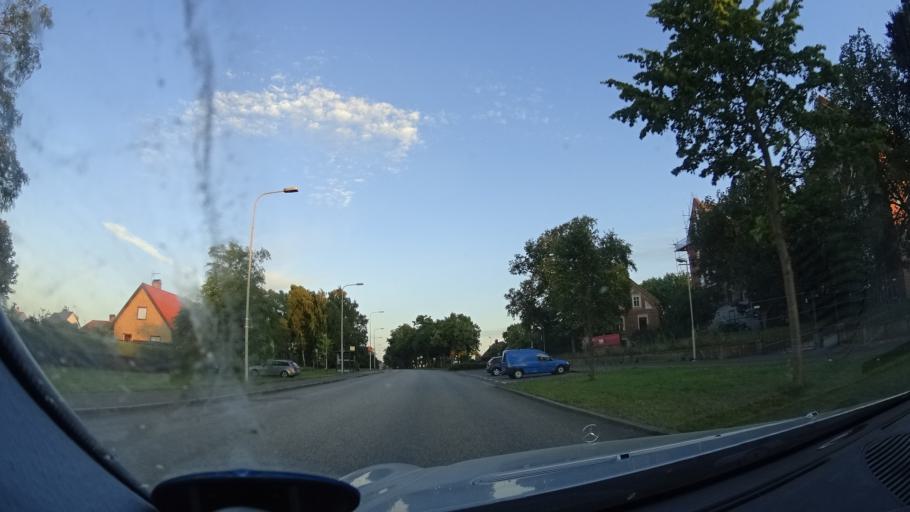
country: SE
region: Skane
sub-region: Kristianstads Kommun
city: Ahus
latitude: 55.9269
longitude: 14.2947
